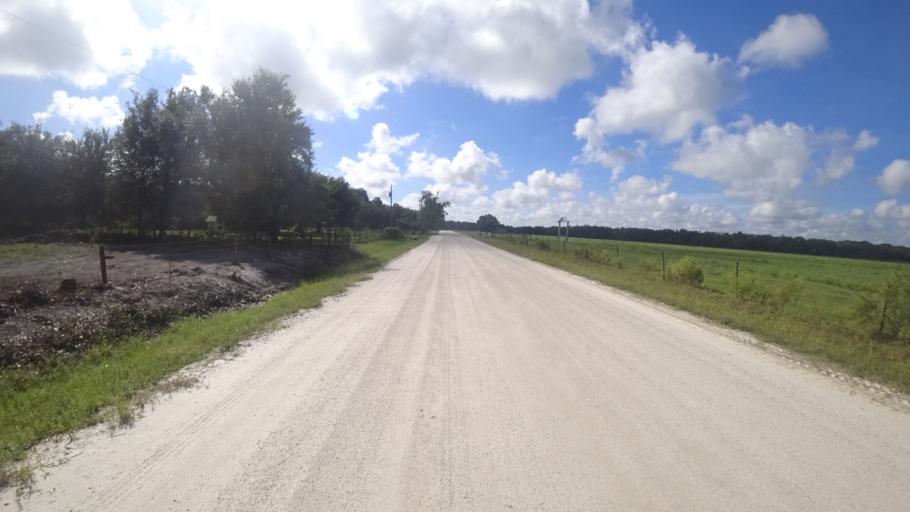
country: US
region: Florida
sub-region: Sarasota County
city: Lake Sarasota
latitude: 27.3327
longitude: -82.2040
